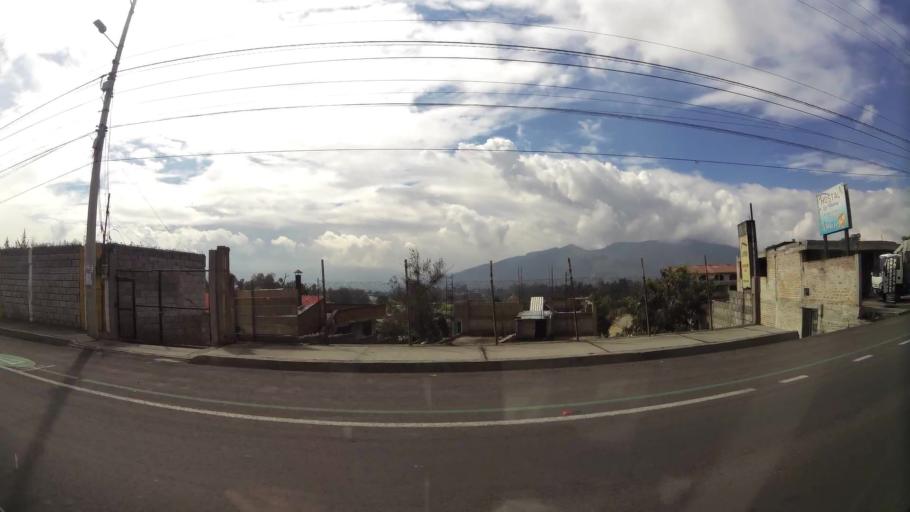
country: EC
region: Pichincha
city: Sangolqui
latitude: -0.3284
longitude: -78.4283
